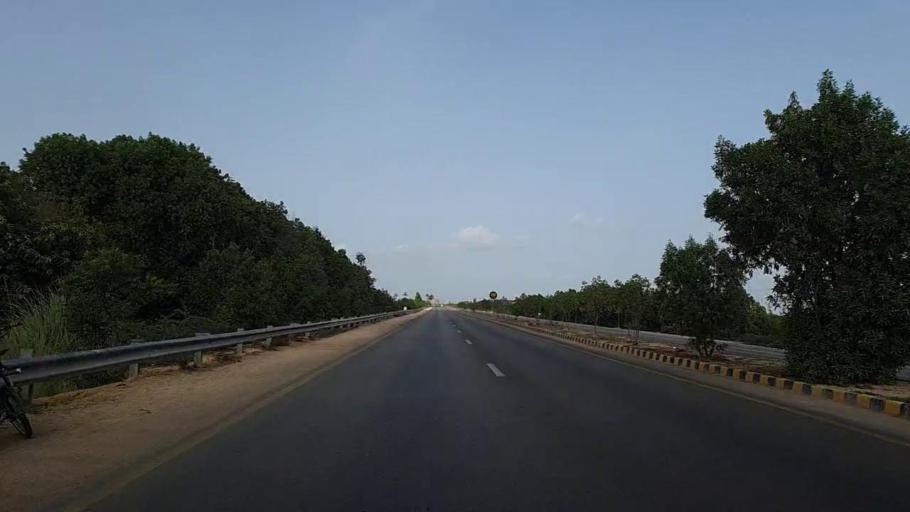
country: PK
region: Sindh
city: Gharo
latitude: 24.7323
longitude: 67.6774
